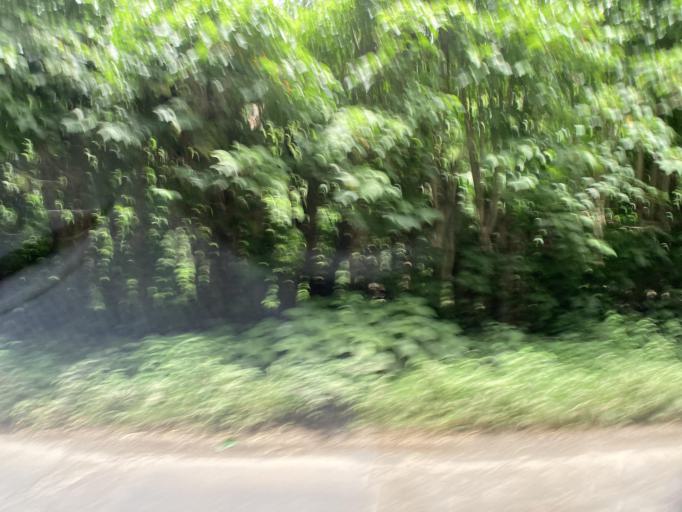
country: GT
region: Guatemala
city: Villa Canales
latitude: 14.4191
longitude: -90.5419
